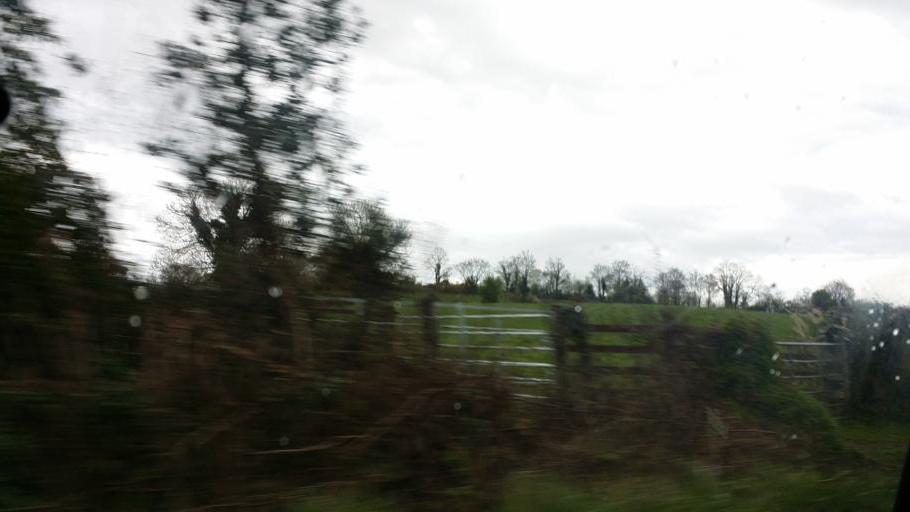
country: IE
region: Ulster
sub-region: An Cabhan
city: Ballyconnell
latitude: 54.1147
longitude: -7.6521
